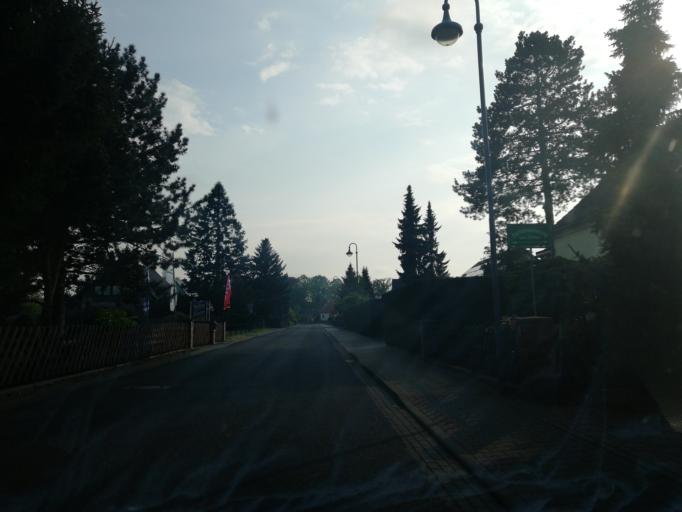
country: DE
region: Brandenburg
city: Calau
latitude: 51.7467
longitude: 13.9776
